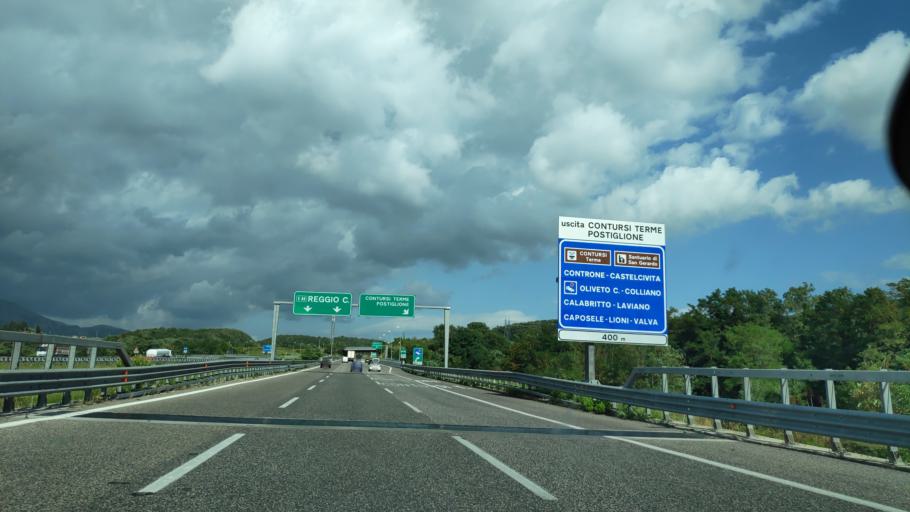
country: IT
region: Campania
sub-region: Provincia di Salerno
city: Contursi Terme
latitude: 40.6284
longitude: 15.2249
